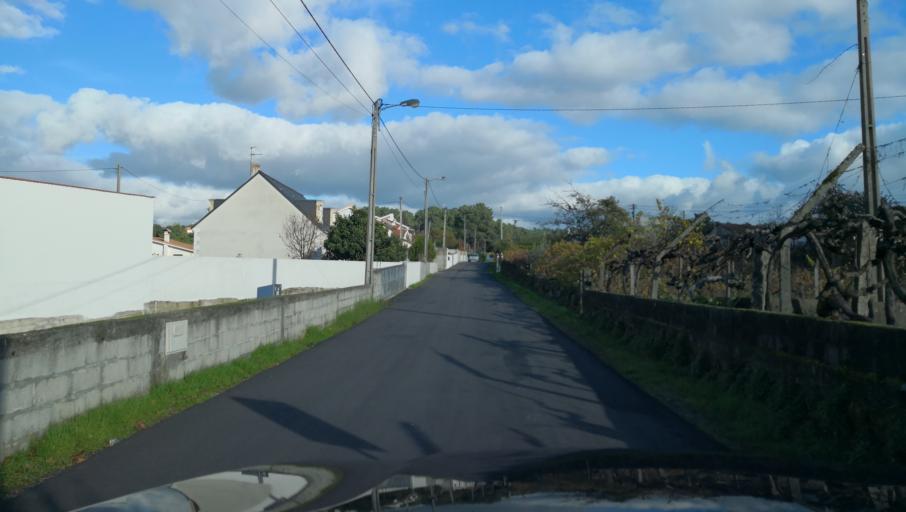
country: PT
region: Vila Real
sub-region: Vila Real
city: Vila Real
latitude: 41.3147
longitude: -7.7231
